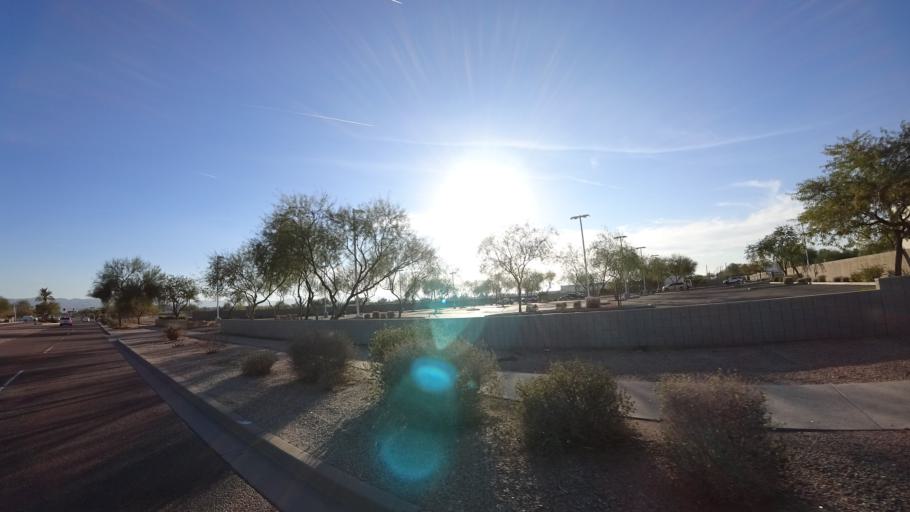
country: US
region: Arizona
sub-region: Maricopa County
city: Phoenix
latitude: 33.4391
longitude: -112.0434
